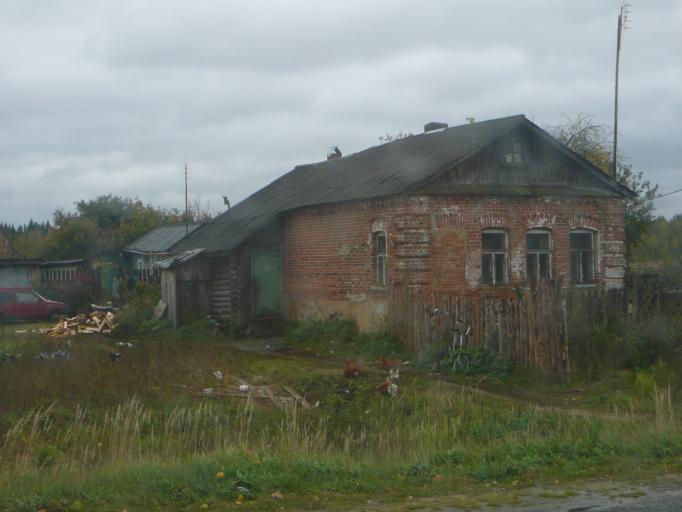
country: RU
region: Moskovskaya
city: Avsyunino
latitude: 55.5329
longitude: 39.2644
